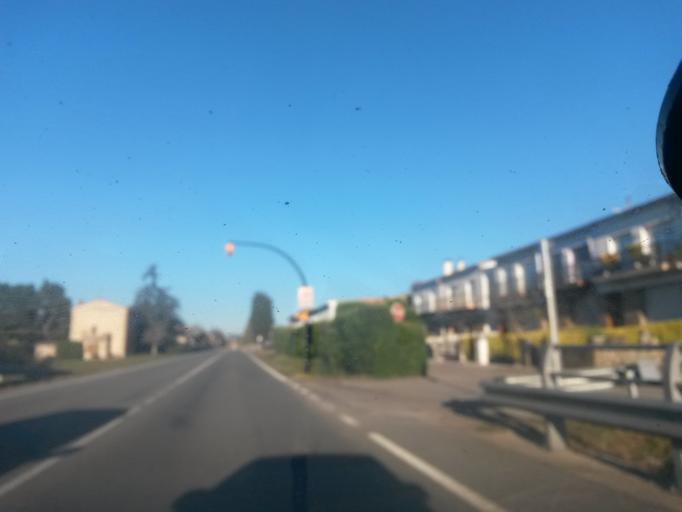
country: ES
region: Catalonia
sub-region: Provincia de Girona
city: Vilablareix
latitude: 41.9491
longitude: 2.7919
